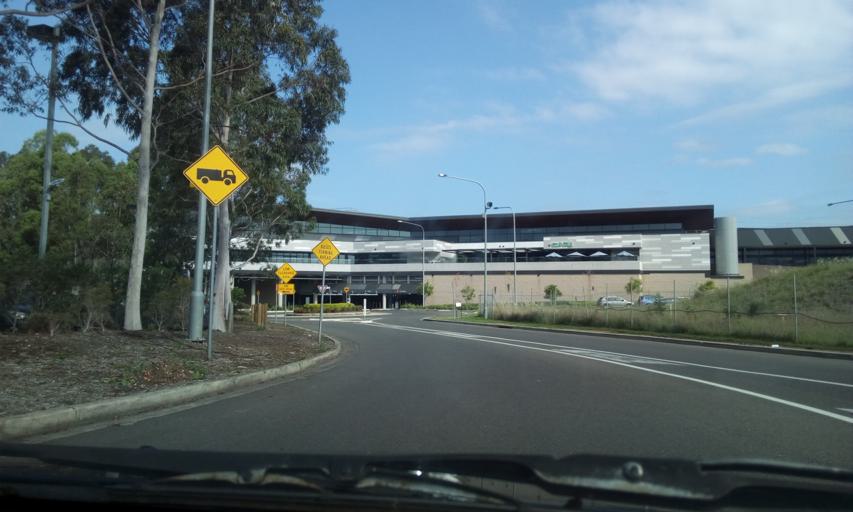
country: AU
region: New South Wales
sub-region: Campbelltown Municipality
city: Glen Alpine
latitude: -34.0740
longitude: 150.7953
